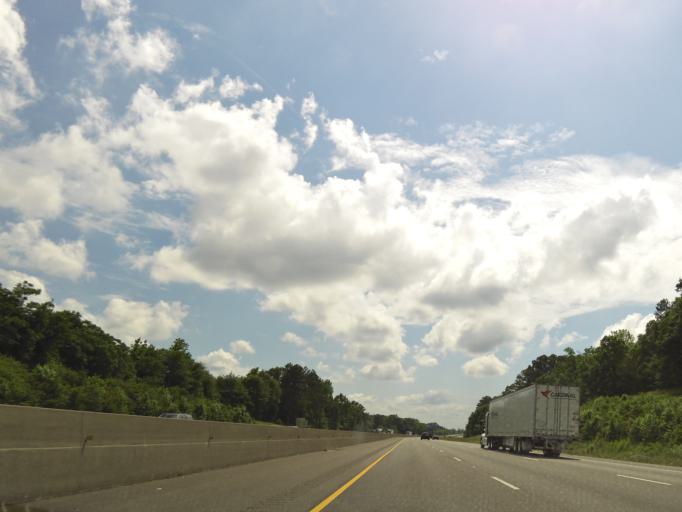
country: US
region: Alabama
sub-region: Calhoun County
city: Oxford
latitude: 33.5973
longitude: -85.8522
